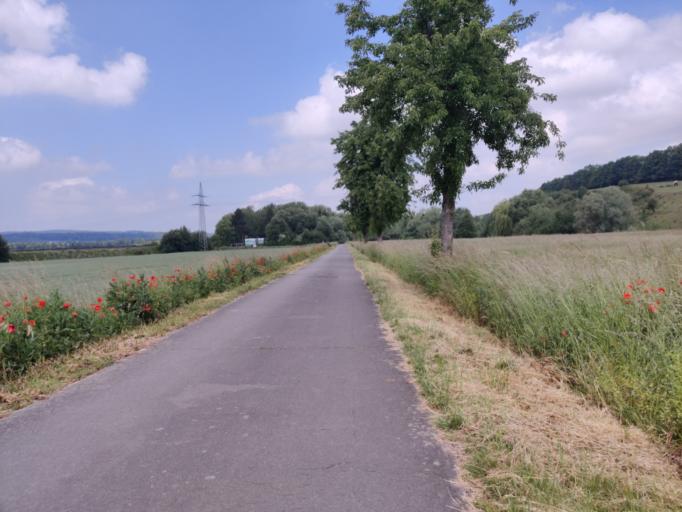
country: DE
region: Lower Saxony
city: Hildesheim
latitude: 52.1229
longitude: 9.9703
